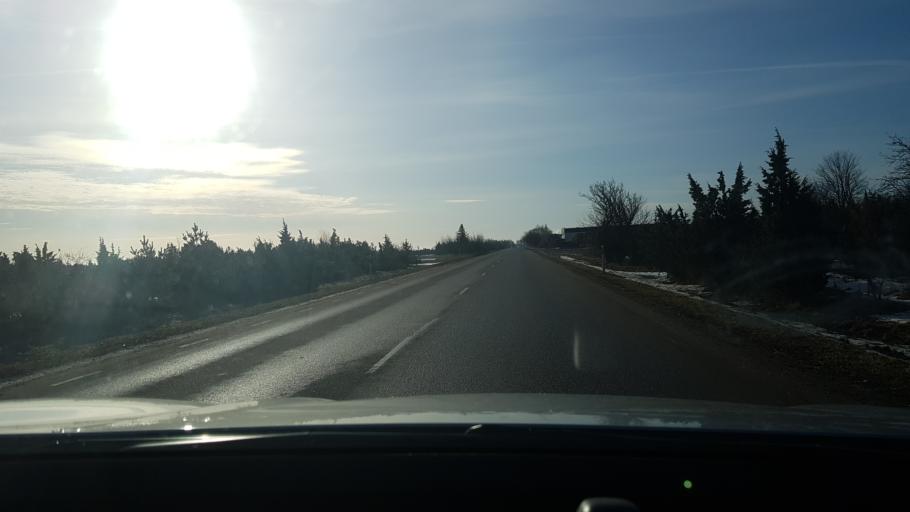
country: EE
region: Saare
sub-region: Kuressaare linn
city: Kuressaare
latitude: 58.2303
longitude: 22.5049
